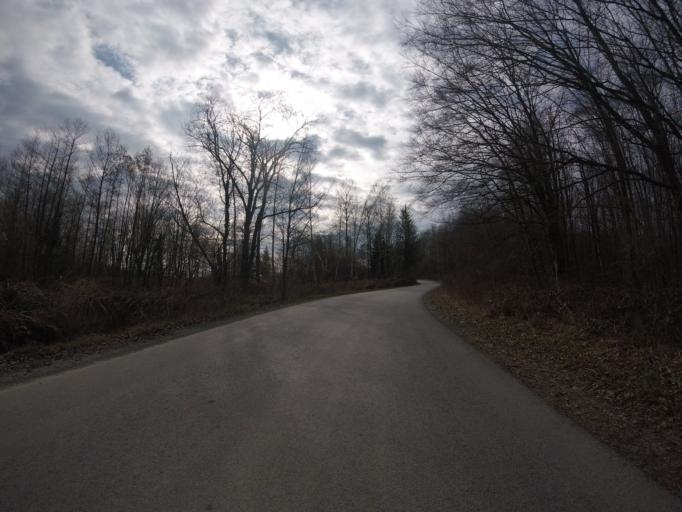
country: HR
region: Sisacko-Moslavacka
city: Glina
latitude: 45.4678
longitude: 16.0341
